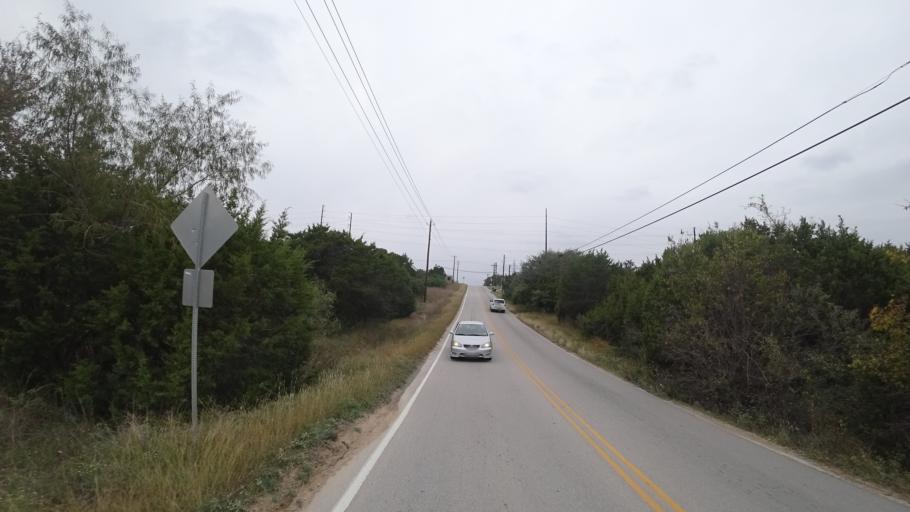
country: US
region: Texas
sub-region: Travis County
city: Lakeway
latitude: 30.3758
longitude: -97.9416
